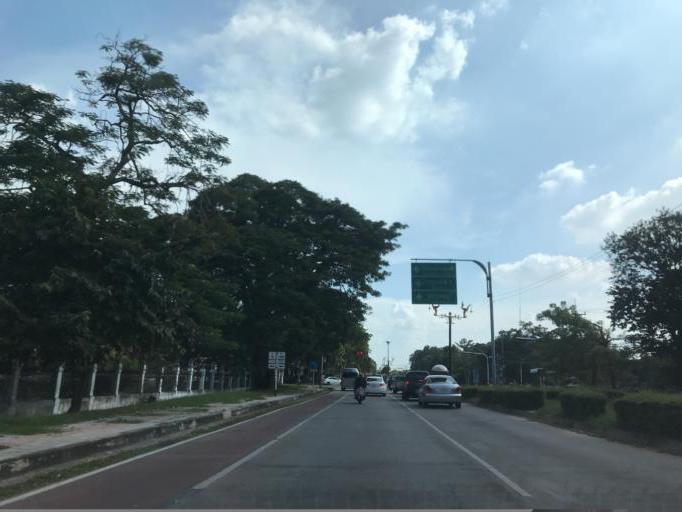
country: TH
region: Phra Nakhon Si Ayutthaya
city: Phra Nakhon Si Ayutthaya
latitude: 14.3506
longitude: 100.5608
